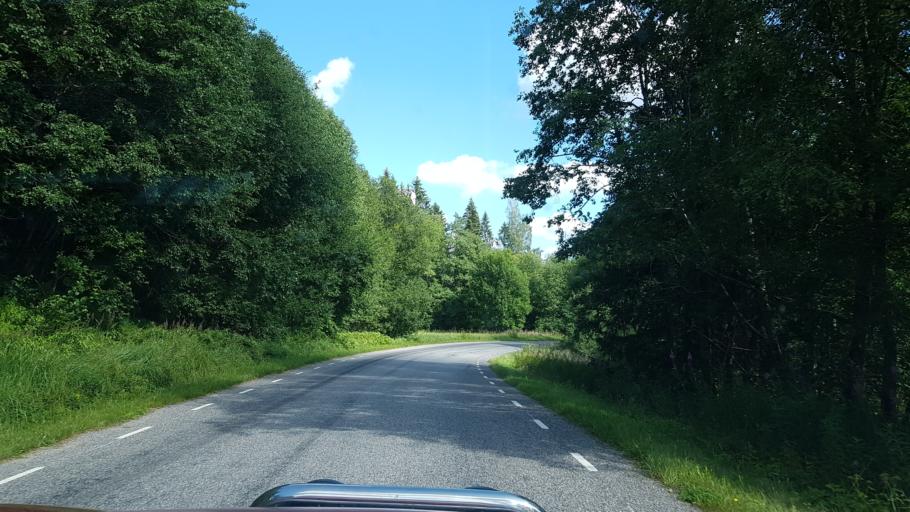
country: EE
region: Vorumaa
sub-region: Voru linn
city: Voru
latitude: 57.7048
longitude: 27.0666
